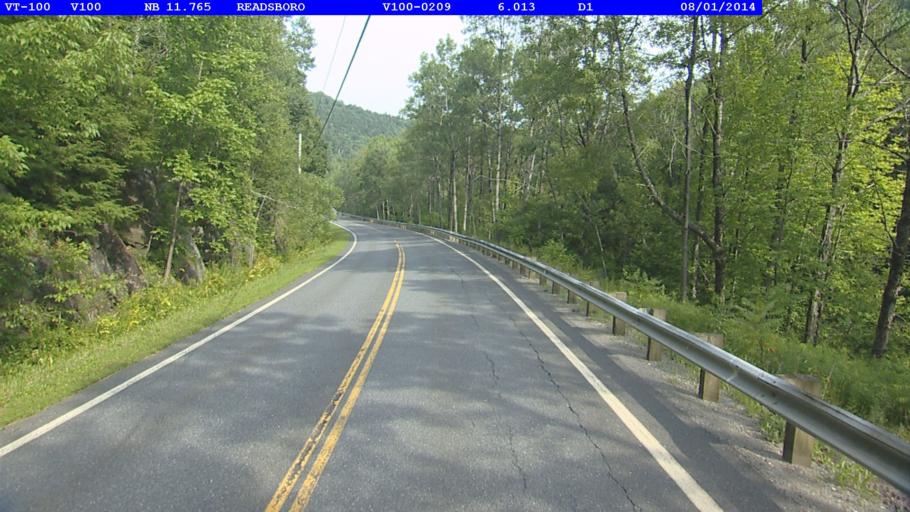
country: US
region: Massachusetts
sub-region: Berkshire County
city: North Adams
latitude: 42.7814
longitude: -72.9585
